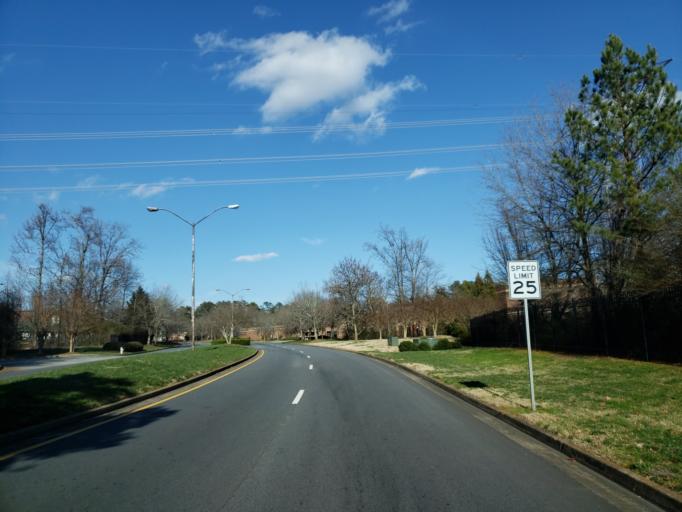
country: US
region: Georgia
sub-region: Cobb County
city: Marietta
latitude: 33.9923
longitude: -84.5239
